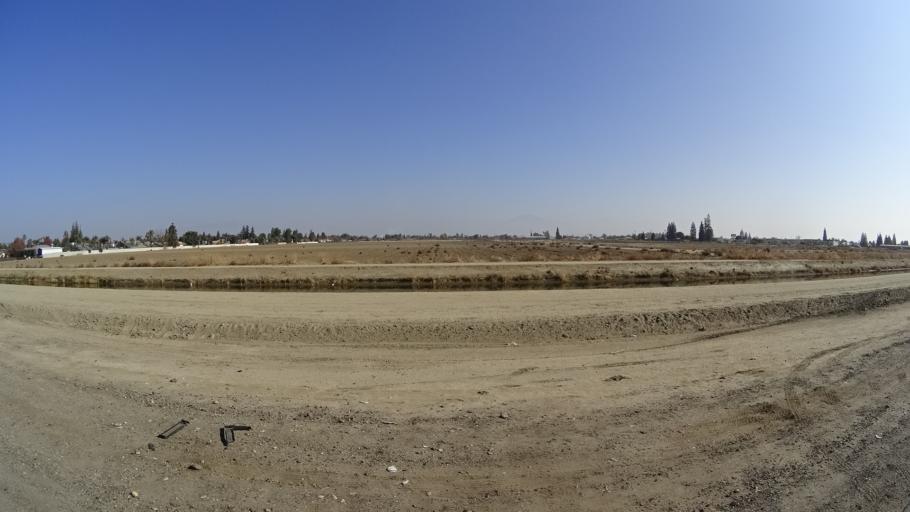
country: US
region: California
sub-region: Kern County
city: Greenfield
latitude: 35.2689
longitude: -119.0213
